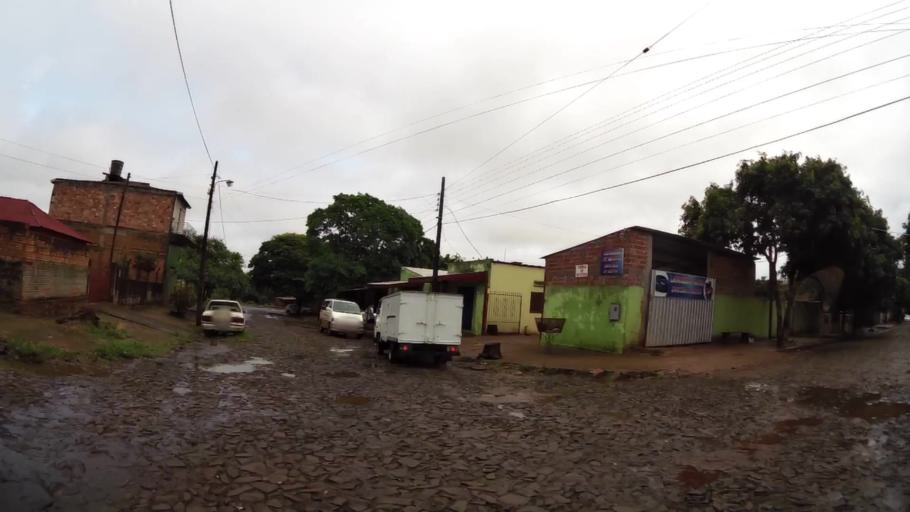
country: PY
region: Alto Parana
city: Presidente Franco
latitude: -25.5141
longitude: -54.6719
